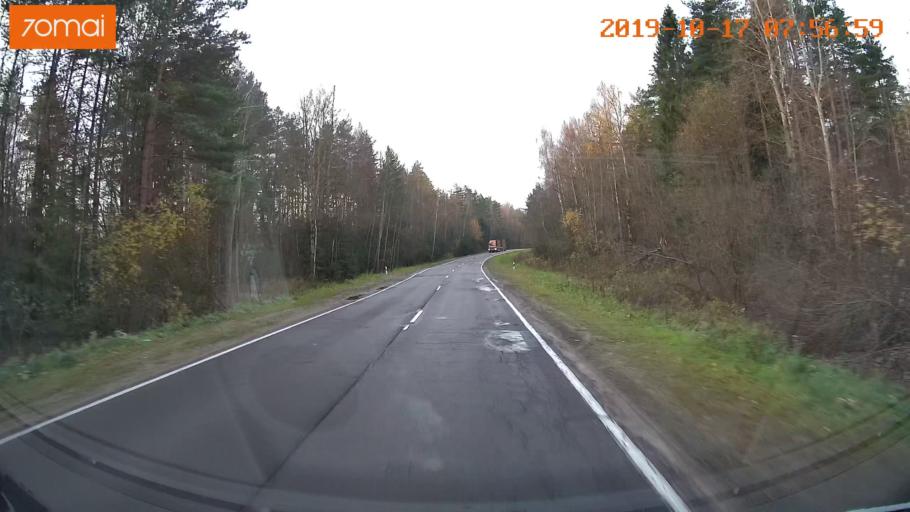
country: RU
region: Vladimir
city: Bavleny
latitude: 56.4163
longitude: 39.5838
